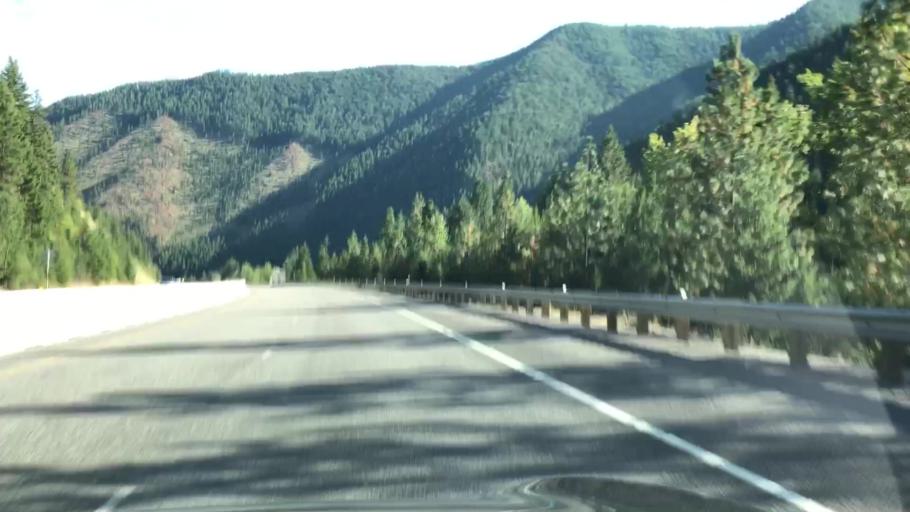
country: US
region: Montana
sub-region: Sanders County
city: Thompson Falls
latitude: 47.3093
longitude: -115.2083
